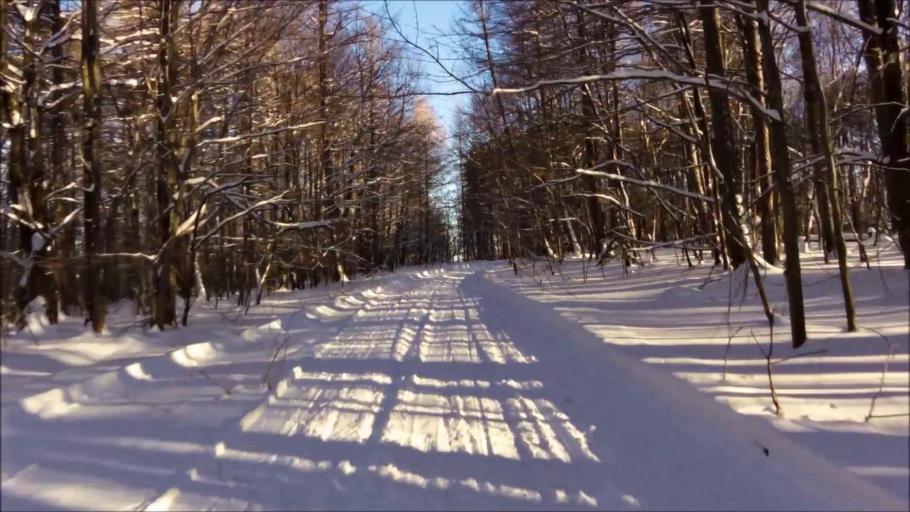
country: US
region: New York
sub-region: Chautauqua County
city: Mayville
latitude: 42.2677
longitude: -79.3815
